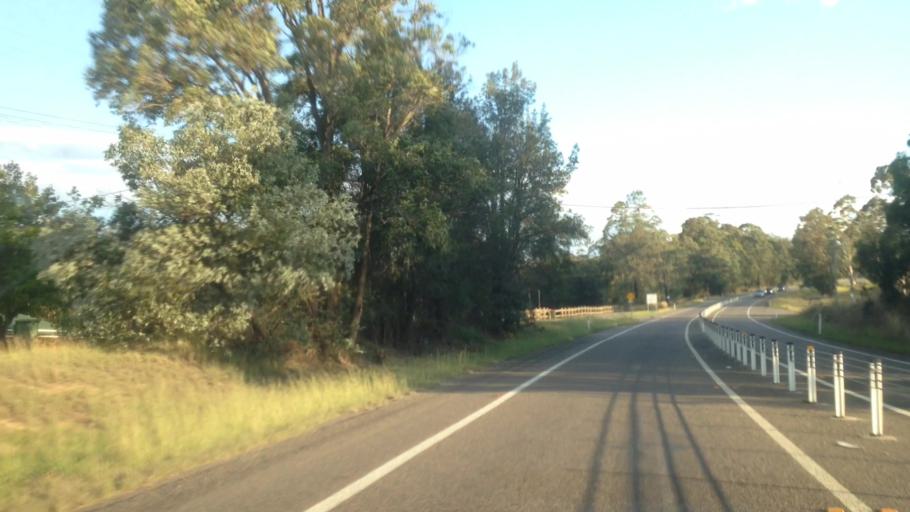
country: AU
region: New South Wales
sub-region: Lake Macquarie Shire
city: Holmesville
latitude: -32.9542
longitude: 151.4808
